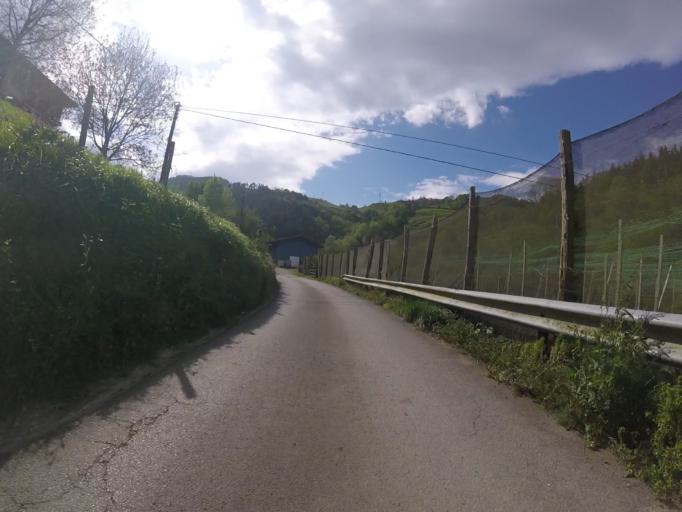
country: ES
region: Basque Country
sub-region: Provincia de Guipuzcoa
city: Aizarnazabal
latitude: 43.2521
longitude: -2.2345
